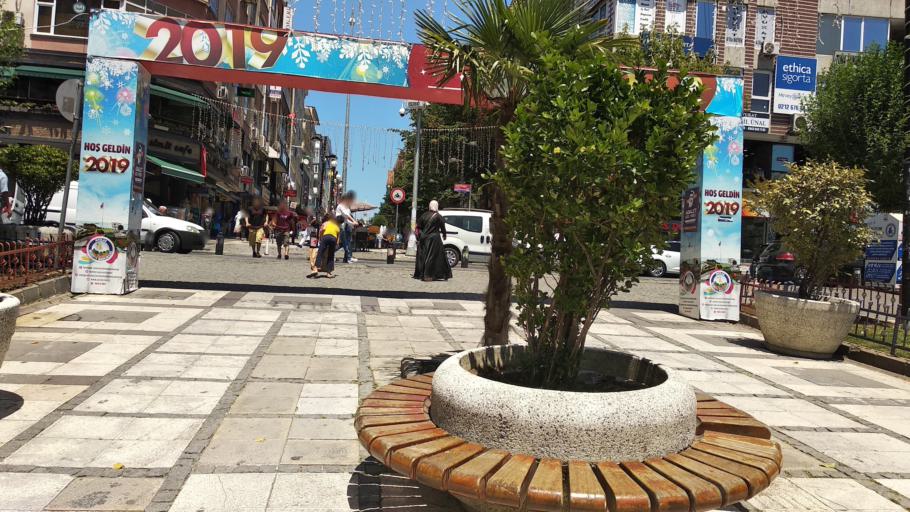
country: TR
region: Istanbul
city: Yakuplu
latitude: 40.9797
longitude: 28.7216
